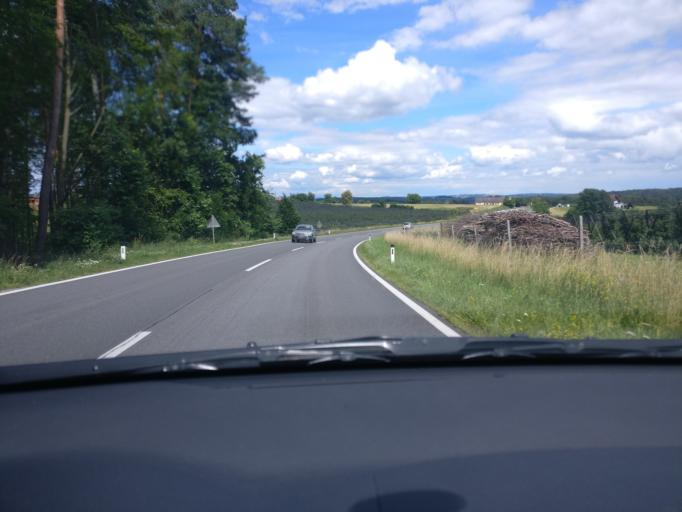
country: AT
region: Styria
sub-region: Politischer Bezirk Hartberg-Fuerstenfeld
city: Kaibing
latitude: 47.2136
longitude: 15.8576
